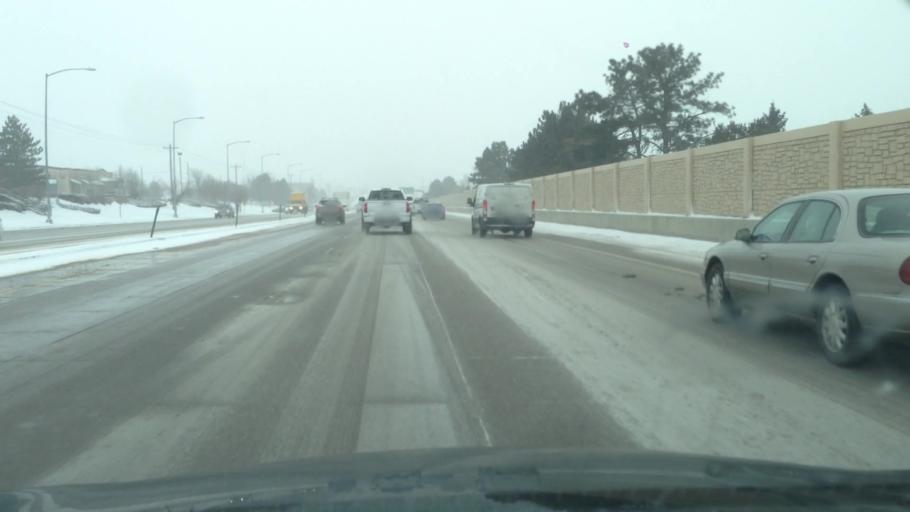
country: US
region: Colorado
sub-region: Arapahoe County
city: Dove Valley
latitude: 39.6018
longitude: -104.8060
